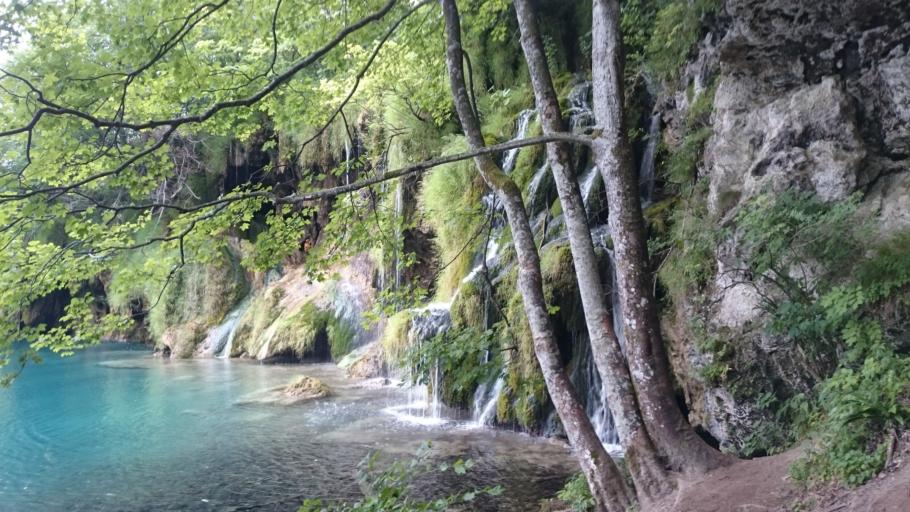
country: HR
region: Licko-Senjska
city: Jezerce
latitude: 44.8806
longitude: 15.6124
